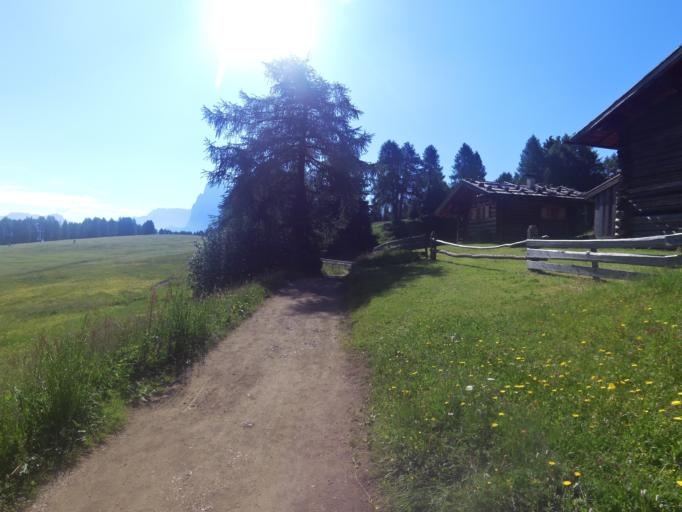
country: IT
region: Trentino-Alto Adige
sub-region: Bolzano
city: Ortisei
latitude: 46.5370
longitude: 11.6429
